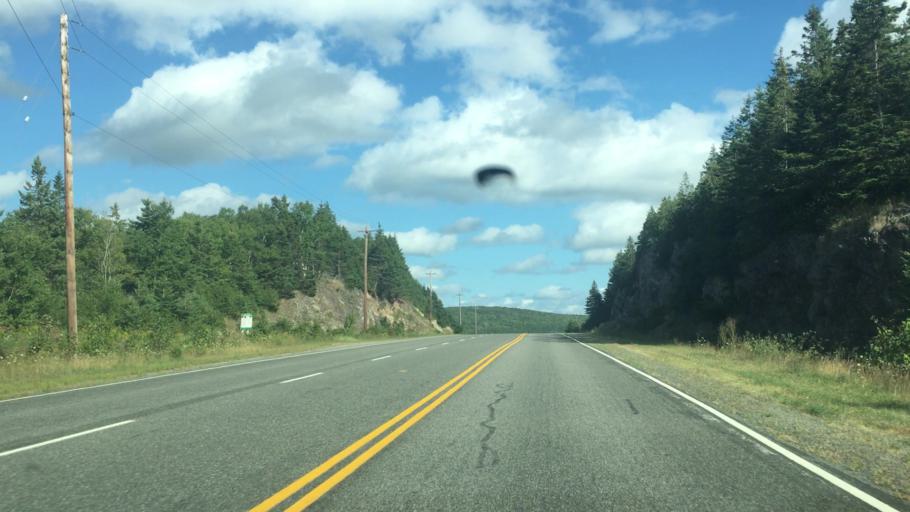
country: CA
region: Nova Scotia
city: Sydney
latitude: 45.8148
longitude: -60.6855
